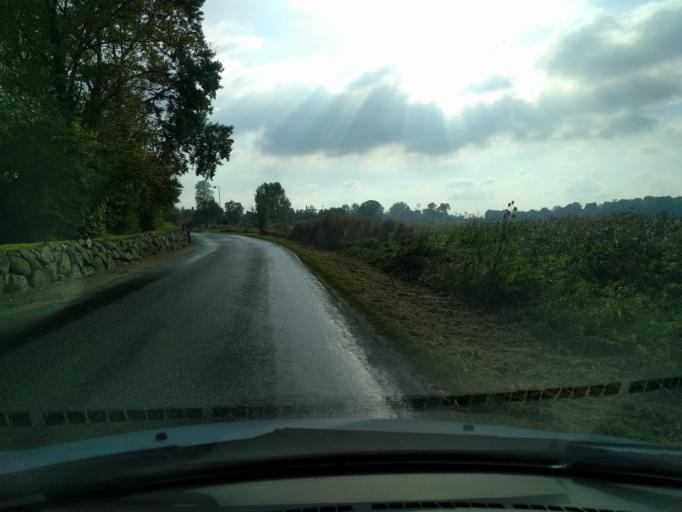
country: DK
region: South Denmark
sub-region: Kerteminde Kommune
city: Munkebo
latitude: 55.4266
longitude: 10.5829
